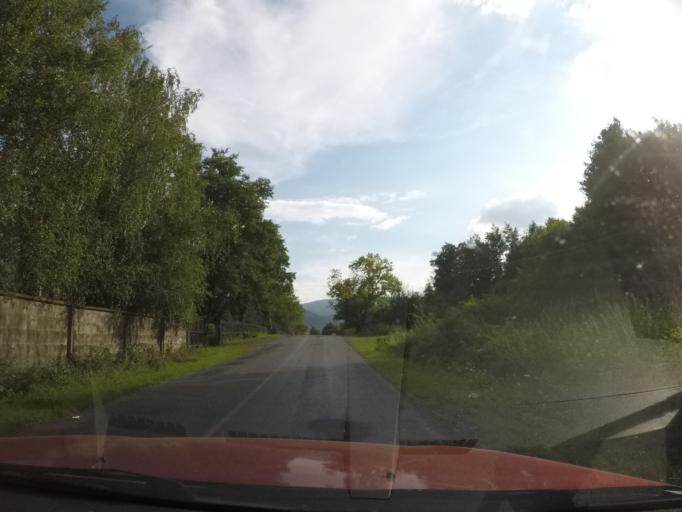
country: UA
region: Zakarpattia
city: Velykyi Bereznyi
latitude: 48.9543
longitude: 22.6113
